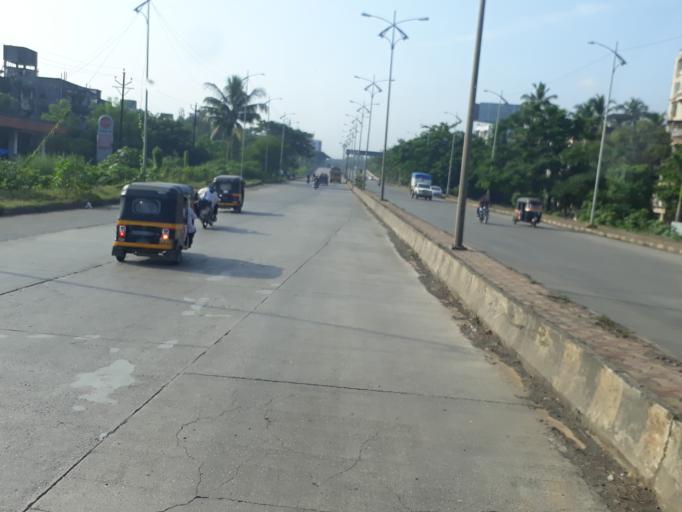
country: IN
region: Maharashtra
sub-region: Raigarh
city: Panvel
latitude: 18.9848
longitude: 73.1159
